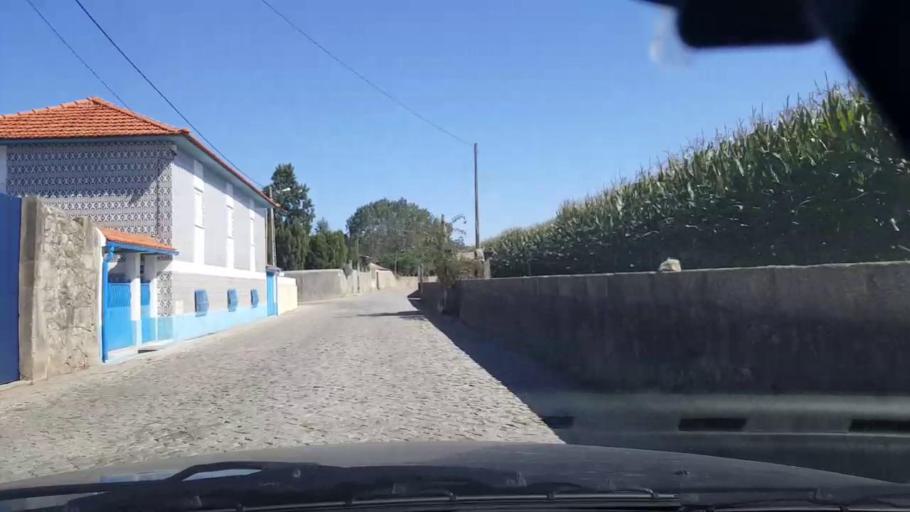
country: PT
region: Porto
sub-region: Vila do Conde
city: Arvore
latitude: 41.3178
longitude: -8.6945
